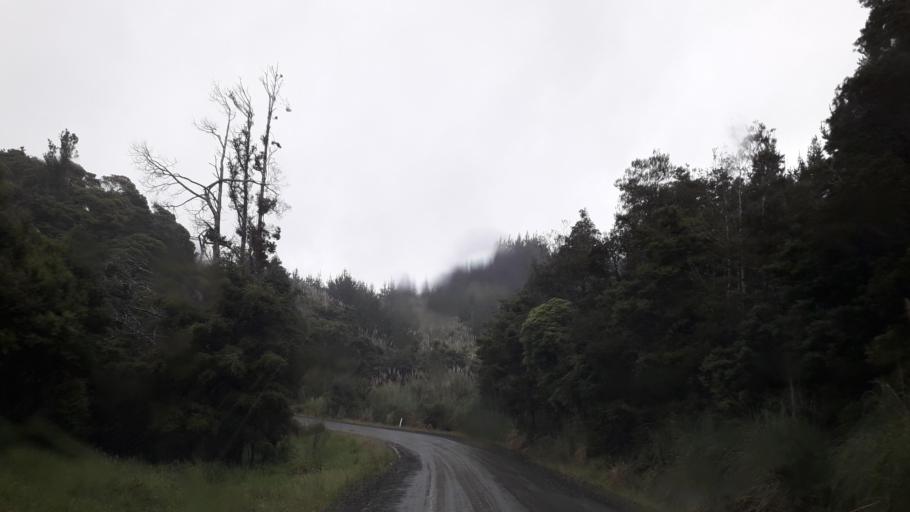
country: NZ
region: Northland
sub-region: Far North District
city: Kaitaia
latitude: -35.3740
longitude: 173.4120
